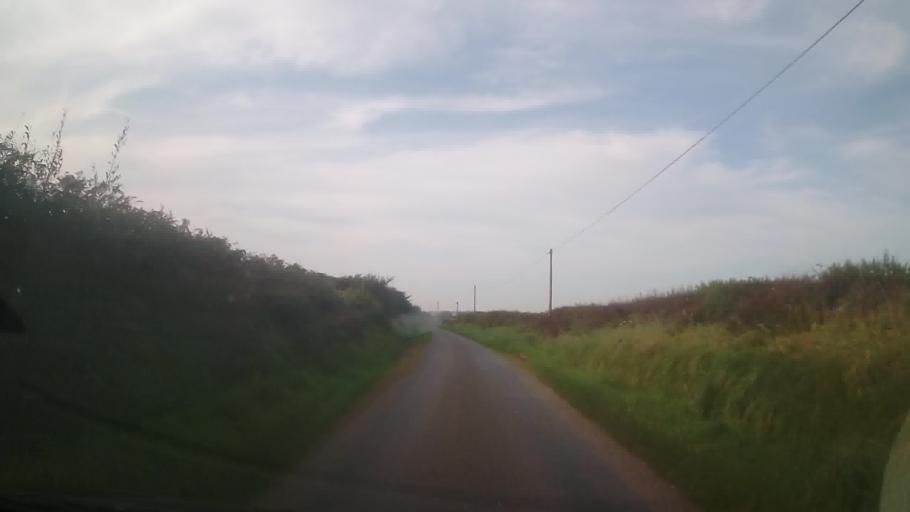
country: GB
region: Wales
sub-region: Pembrokeshire
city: Camrose
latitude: 51.8834
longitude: -5.0518
